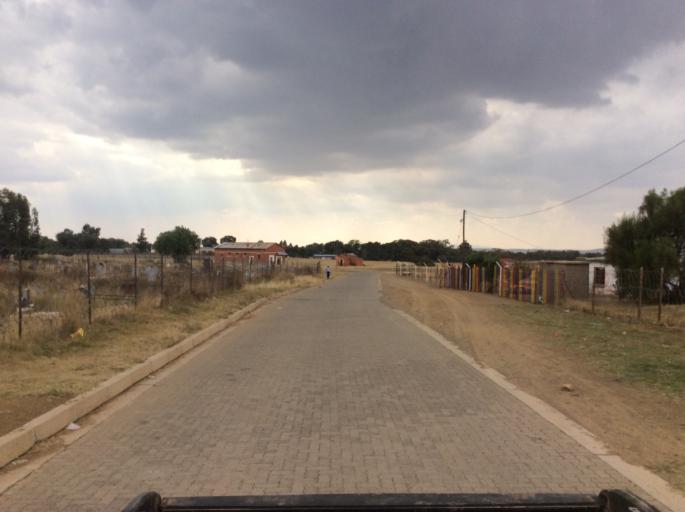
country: ZA
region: Orange Free State
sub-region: Xhariep District Municipality
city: Dewetsdorp
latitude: -29.5827
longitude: 26.6743
